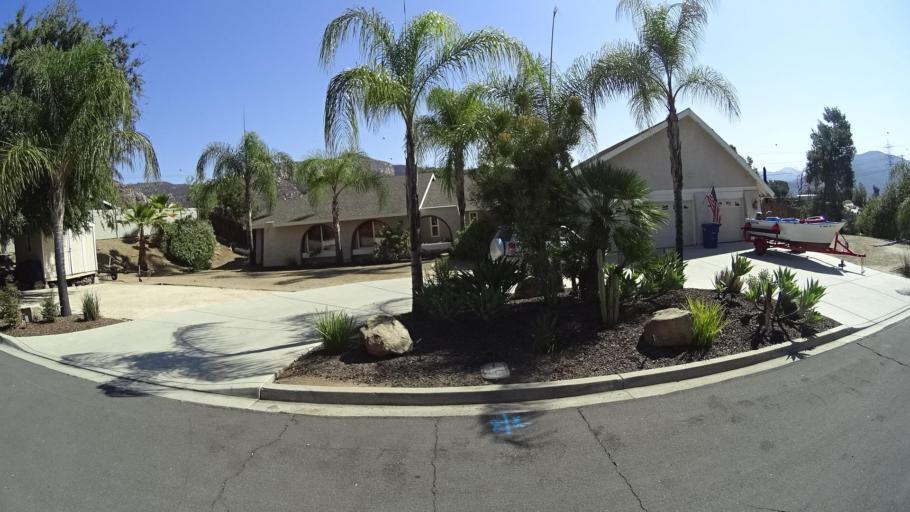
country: US
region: California
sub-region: San Diego County
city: Granite Hills
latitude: 32.7888
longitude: -116.8946
